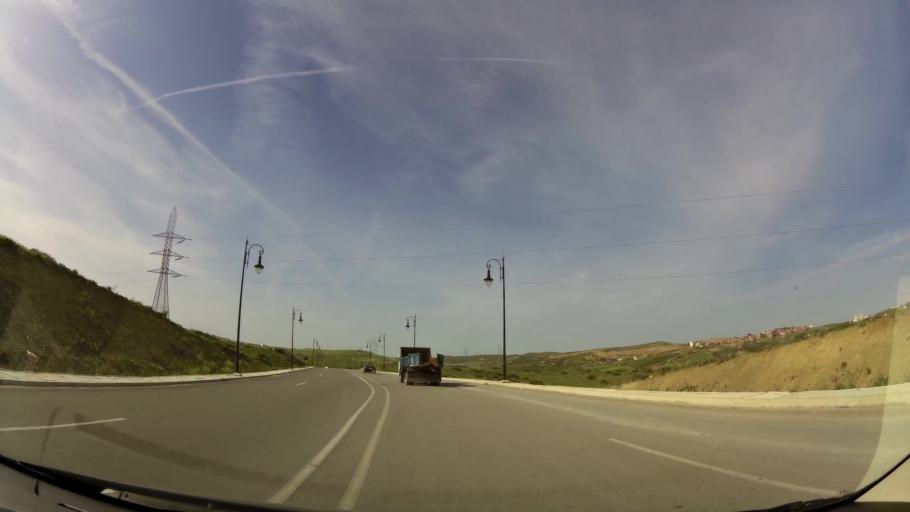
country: MA
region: Tanger-Tetouan
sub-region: Tanger-Assilah
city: Tangier
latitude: 35.7178
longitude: -5.7723
